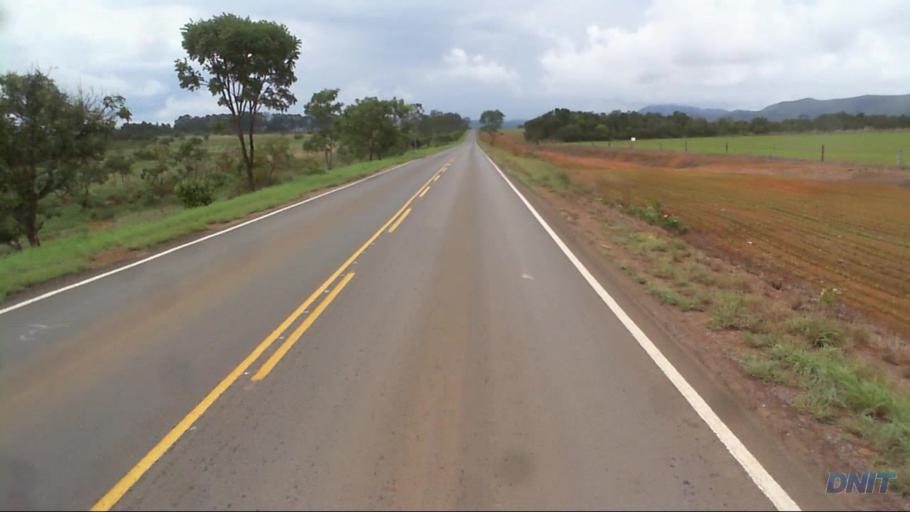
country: BR
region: Goias
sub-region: Padre Bernardo
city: Padre Bernardo
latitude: -15.3101
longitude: -48.2273
